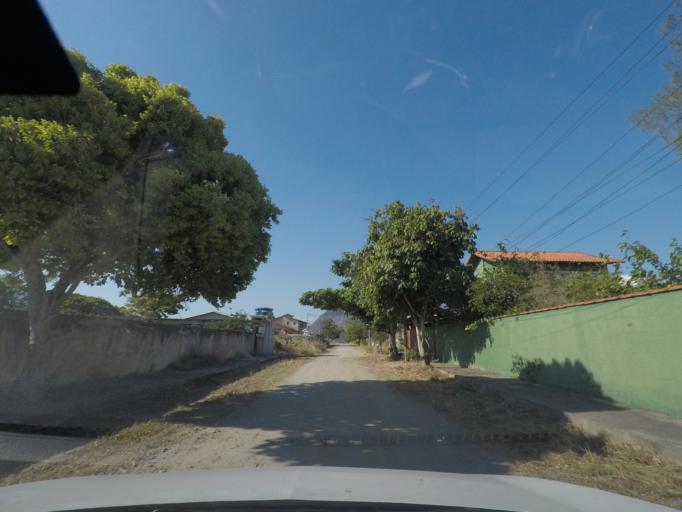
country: BR
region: Rio de Janeiro
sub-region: Marica
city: Marica
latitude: -22.9694
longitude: -42.9118
